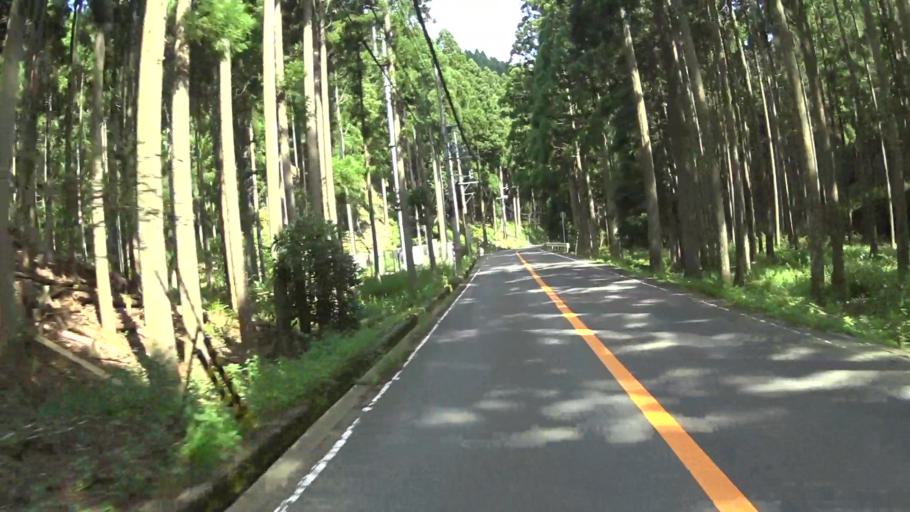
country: JP
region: Kyoto
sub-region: Kyoto-shi
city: Kamigyo-ku
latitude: 35.2484
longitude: 135.6493
